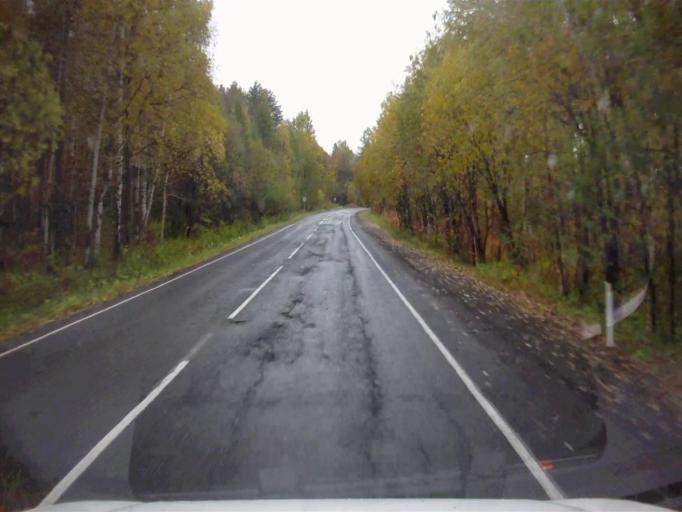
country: RU
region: Chelyabinsk
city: Verkhniy Ufaley
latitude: 56.0432
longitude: 60.0997
